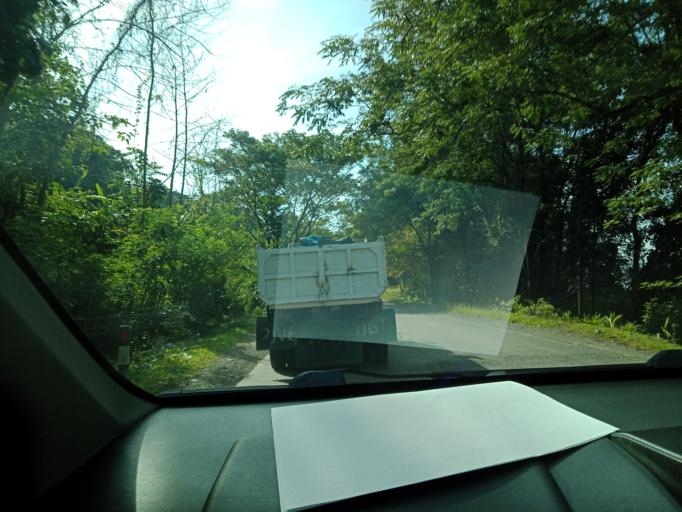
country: ID
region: South Sulawesi
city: Makassar
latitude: -5.2437
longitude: 119.6214
